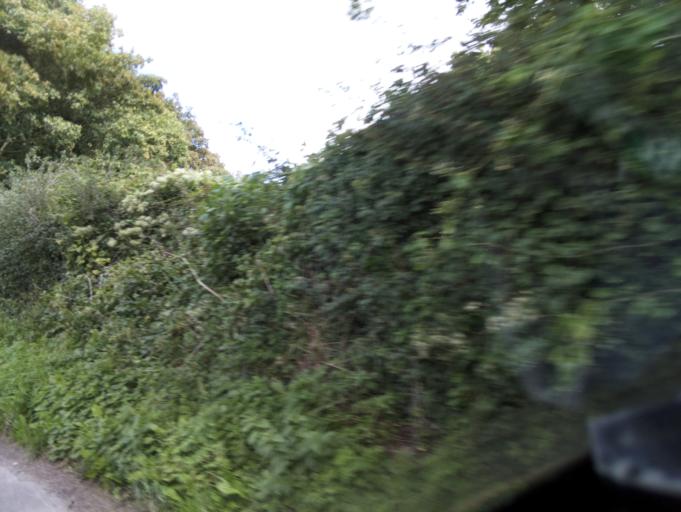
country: GB
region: England
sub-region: Wiltshire
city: Colerne
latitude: 51.4348
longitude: -2.2606
